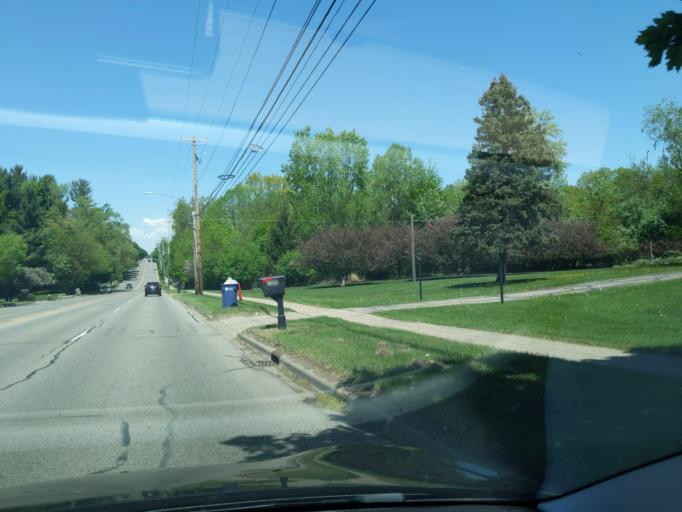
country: US
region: Michigan
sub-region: Kent County
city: East Grand Rapids
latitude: 42.9187
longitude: -85.6085
